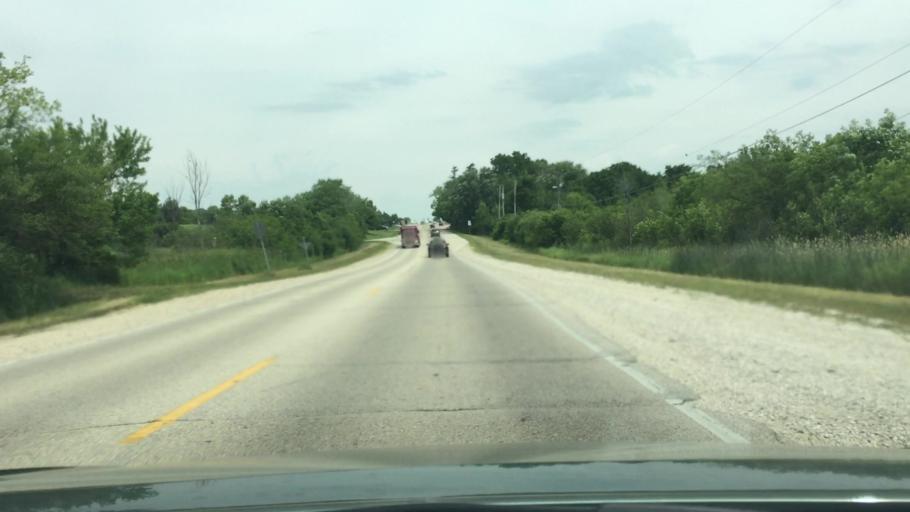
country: US
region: Wisconsin
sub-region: Waukesha County
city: Hartland
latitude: 43.0995
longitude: -88.3134
